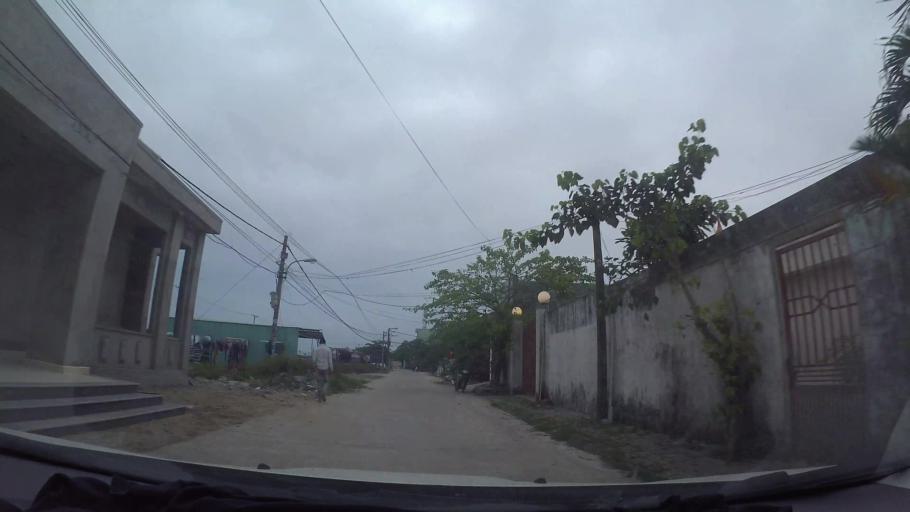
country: VN
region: Da Nang
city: Lien Chieu
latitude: 16.0859
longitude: 108.1566
